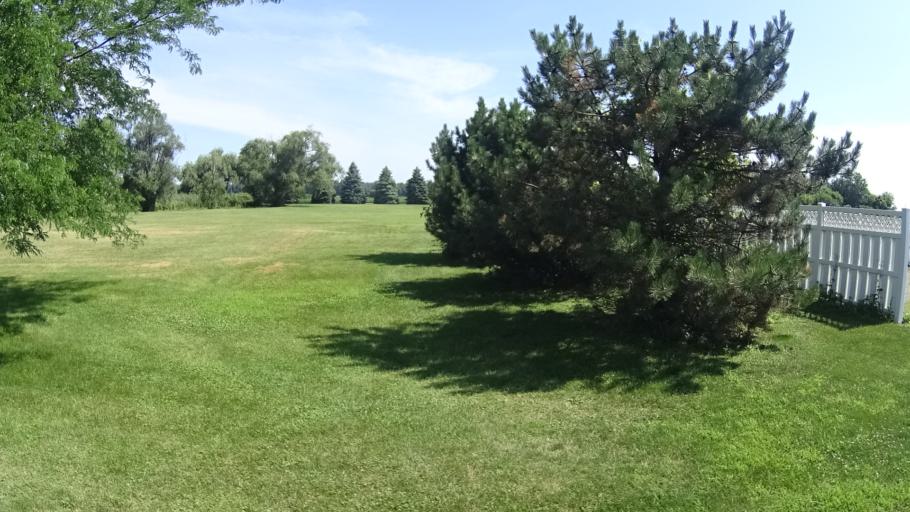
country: US
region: Ohio
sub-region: Erie County
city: Sandusky
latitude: 41.4207
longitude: -82.8078
